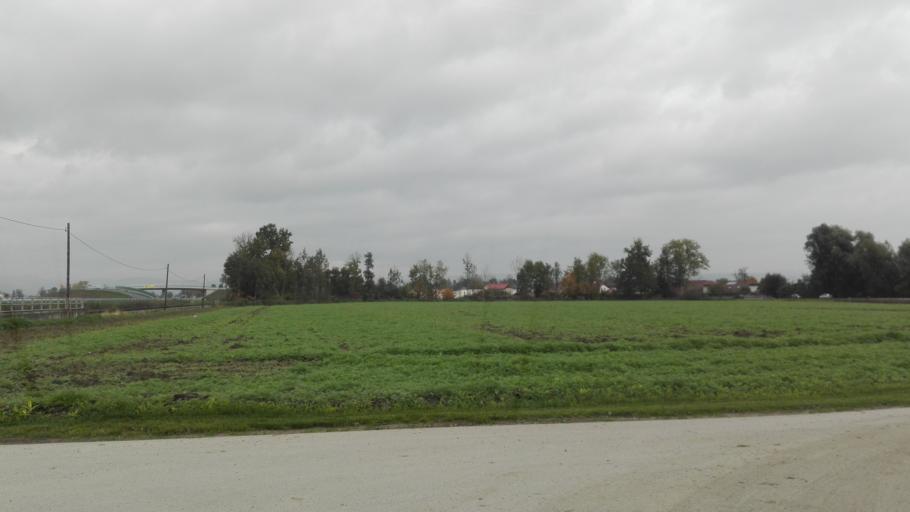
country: AT
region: Upper Austria
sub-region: Politischer Bezirk Urfahr-Umgebung
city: Feldkirchen an der Donau
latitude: 48.3217
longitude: 14.0104
